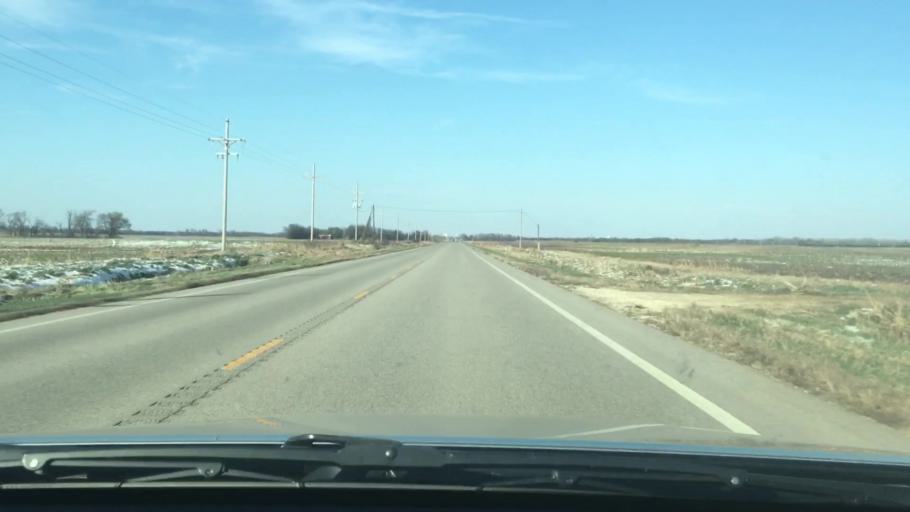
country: US
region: Kansas
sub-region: Rice County
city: Lyons
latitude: 38.2787
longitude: -98.2022
